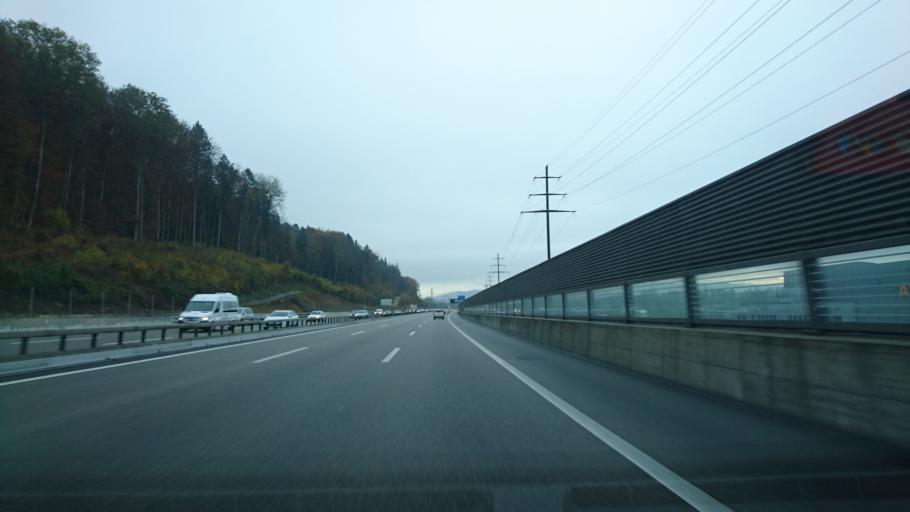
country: CH
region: Aargau
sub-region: Bezirk Zofingen
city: Rothrist
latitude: 47.3129
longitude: 7.8767
